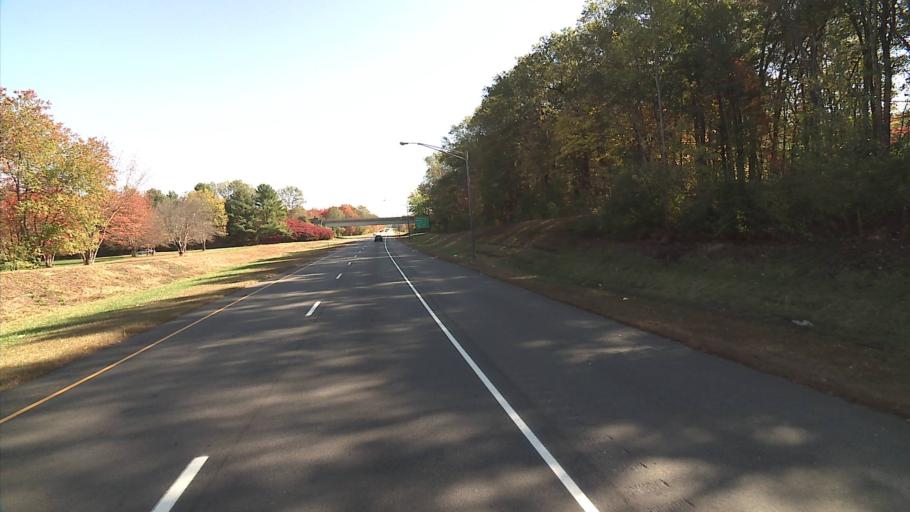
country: US
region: Connecticut
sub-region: Windham County
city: Willimantic
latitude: 41.7288
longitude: -72.2300
